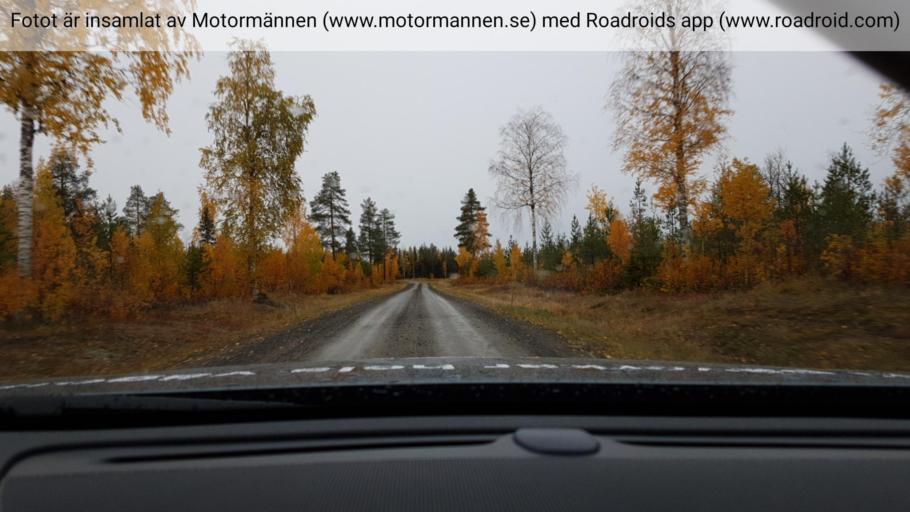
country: SE
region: Norrbotten
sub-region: Pajala Kommun
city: Pajala
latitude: 67.0439
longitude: 22.8419
